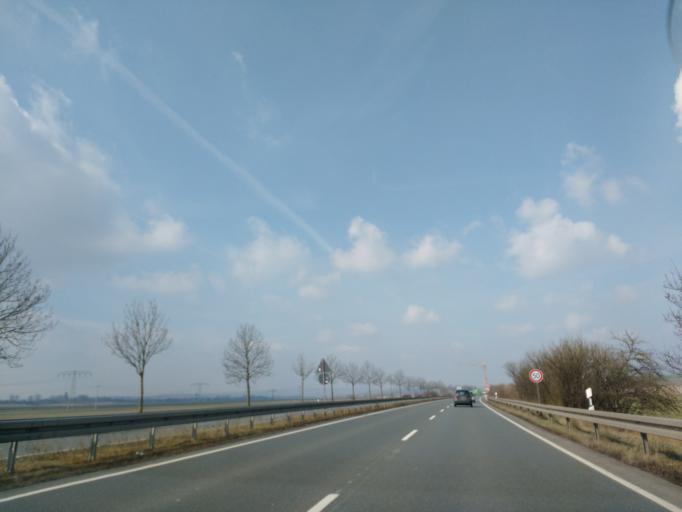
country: DE
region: Saxony-Anhalt
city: Wansleben
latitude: 51.4730
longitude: 11.7300
